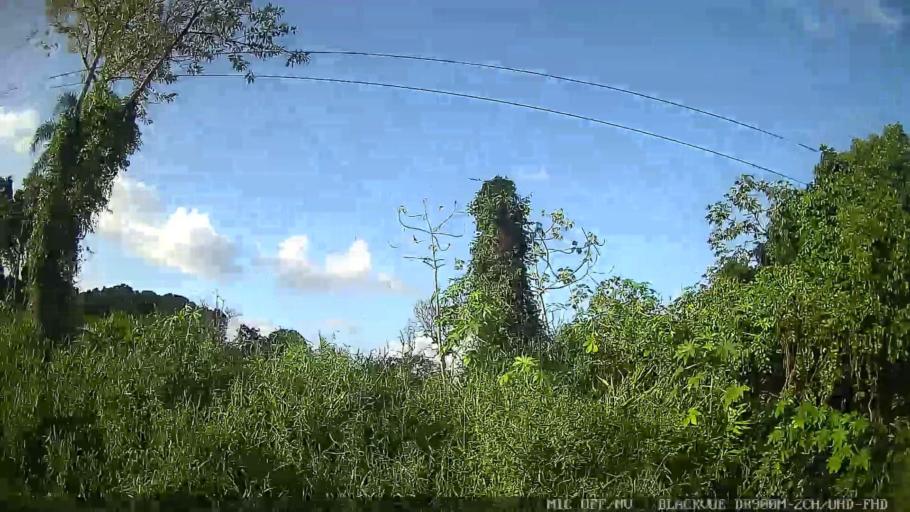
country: BR
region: Sao Paulo
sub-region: Itanhaem
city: Itanhaem
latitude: -24.1356
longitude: -46.7181
